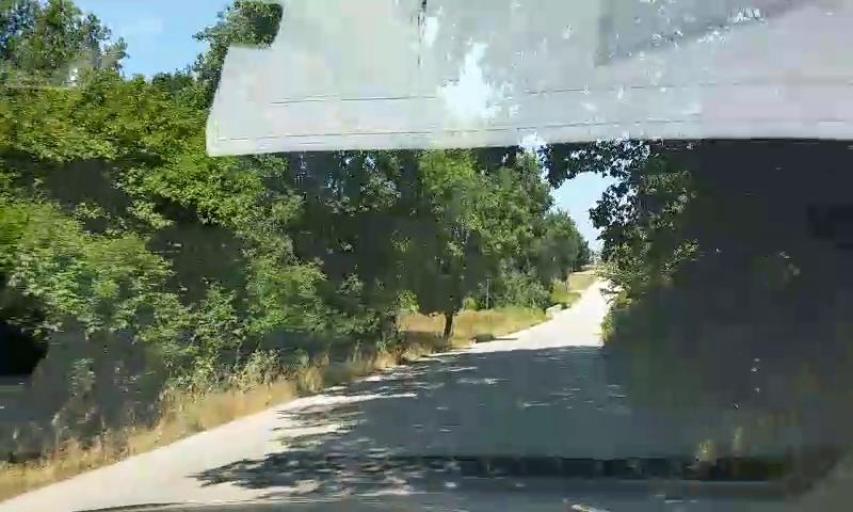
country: IT
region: Molise
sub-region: Provincia di Campobasso
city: San Giacomo degli Schiavoni
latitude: 41.9632
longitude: 14.9003
